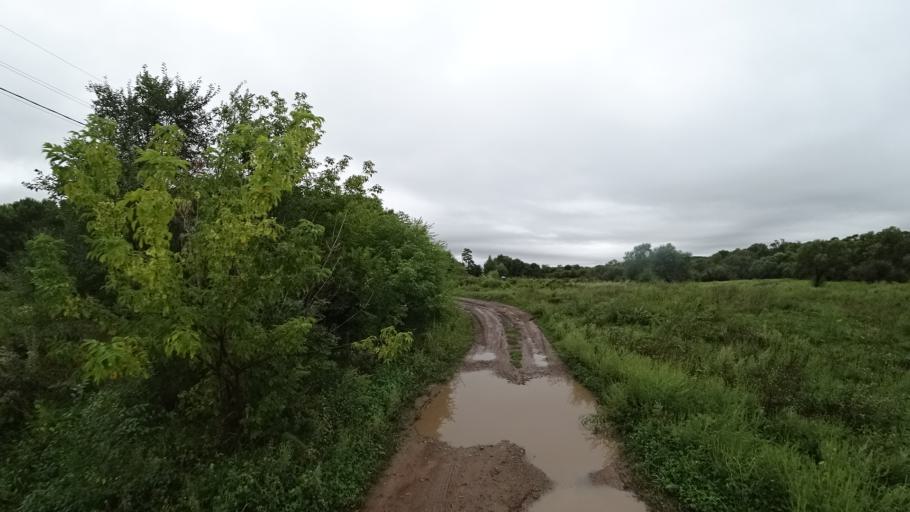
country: RU
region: Primorskiy
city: Monastyrishche
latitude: 44.2718
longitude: 132.4052
